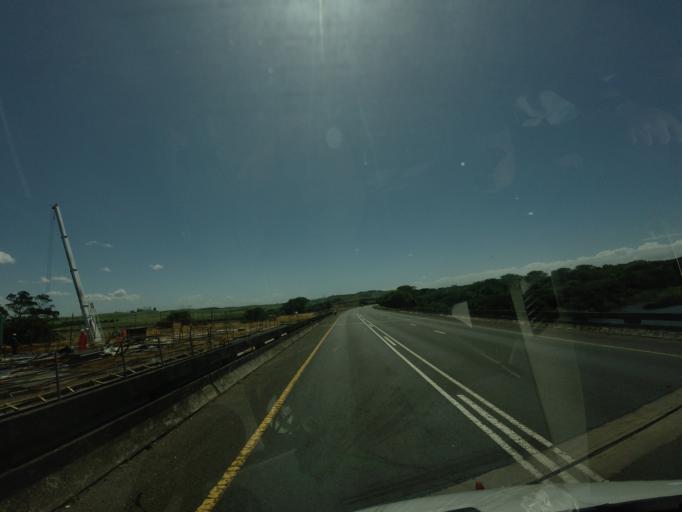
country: ZA
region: KwaZulu-Natal
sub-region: uThungulu District Municipality
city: eSikhawini
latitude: -28.9326
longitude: 31.7569
